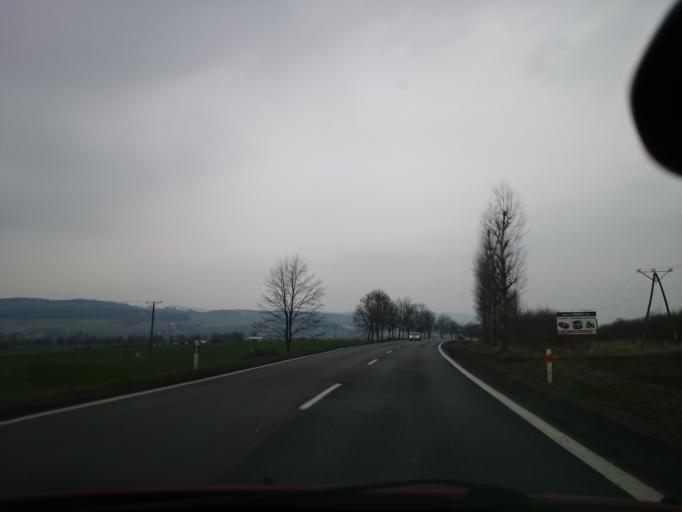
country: PL
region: Lower Silesian Voivodeship
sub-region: Powiat klodzki
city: Klodzko
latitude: 50.4498
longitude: 16.6309
